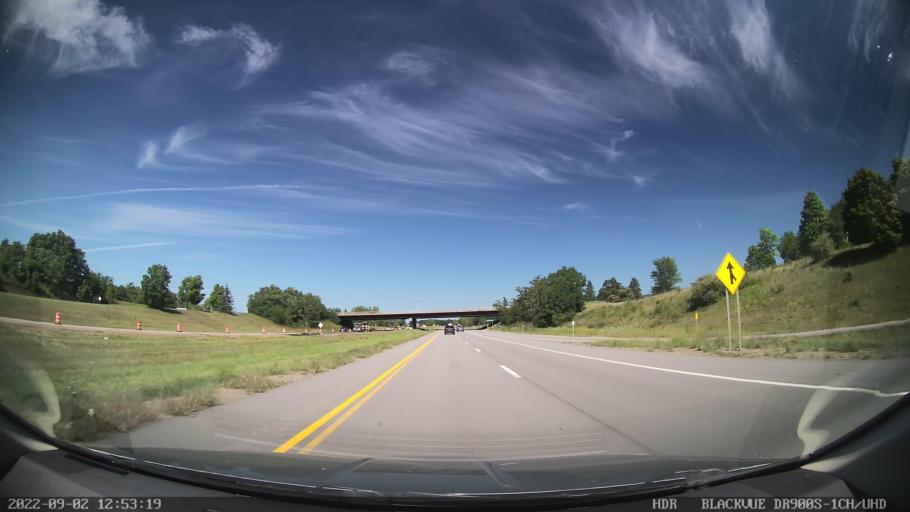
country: US
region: New York
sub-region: Livingston County
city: Avon
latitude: 42.9041
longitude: -77.6951
